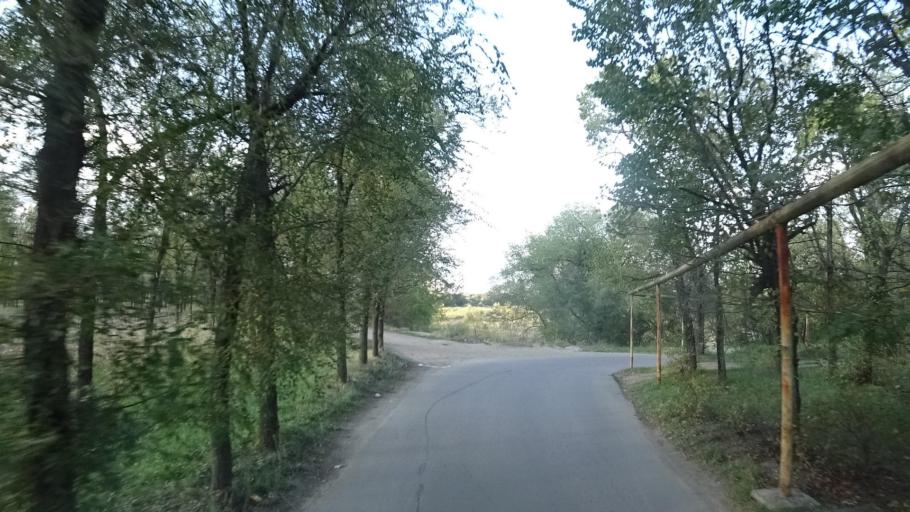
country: KZ
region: Almaty Oblysy
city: Pervomayskiy
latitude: 43.3318
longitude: 76.9871
